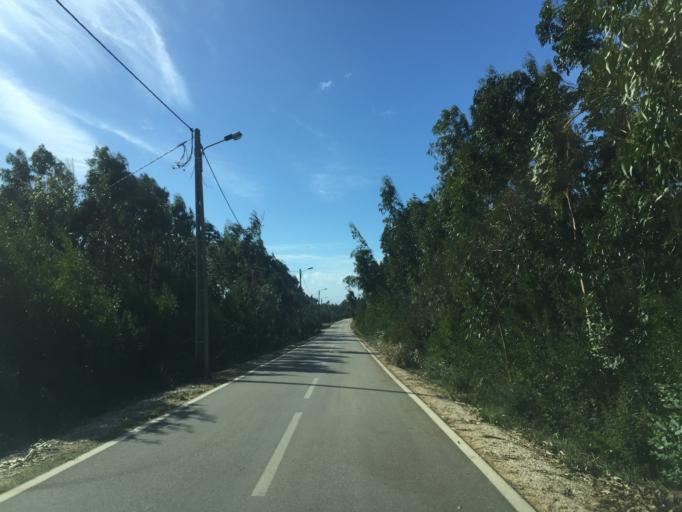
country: PT
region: Coimbra
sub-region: Figueira da Foz
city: Buarcos
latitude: 40.1896
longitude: -8.8925
